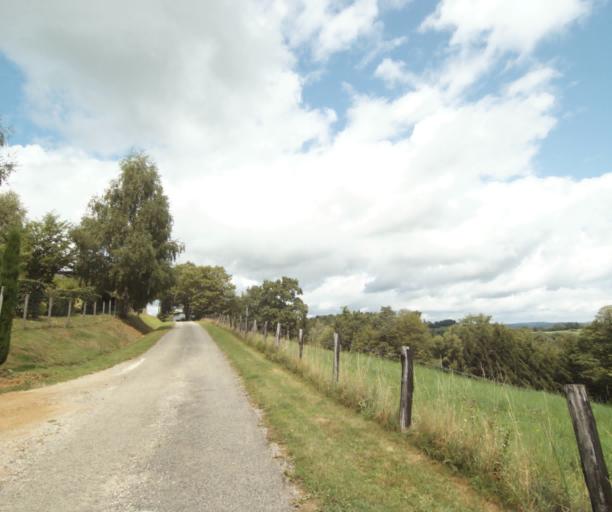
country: FR
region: Limousin
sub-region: Departement de la Correze
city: Laguenne
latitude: 45.2137
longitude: 1.8283
